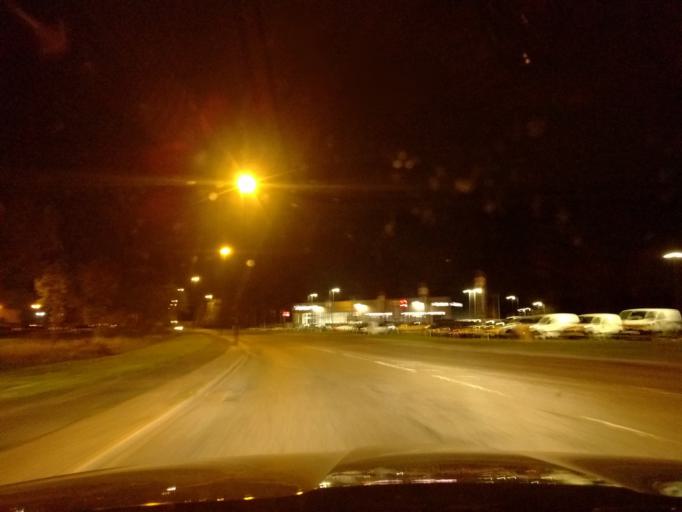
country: GB
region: England
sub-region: Borough of North Tyneside
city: Wallsend
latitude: 55.0151
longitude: -1.5483
